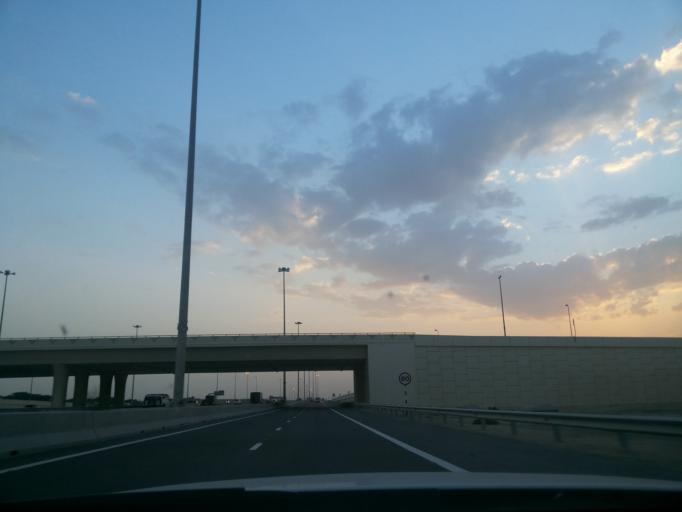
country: AE
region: Abu Dhabi
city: Abu Dhabi
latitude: 24.6868
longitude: 54.7731
